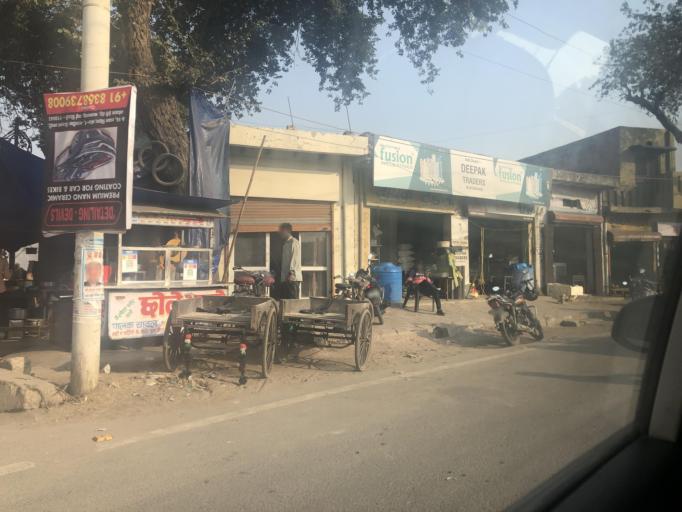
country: IN
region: Haryana
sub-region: Jhajjar
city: Bahadurgarh
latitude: 28.6182
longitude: 76.9753
